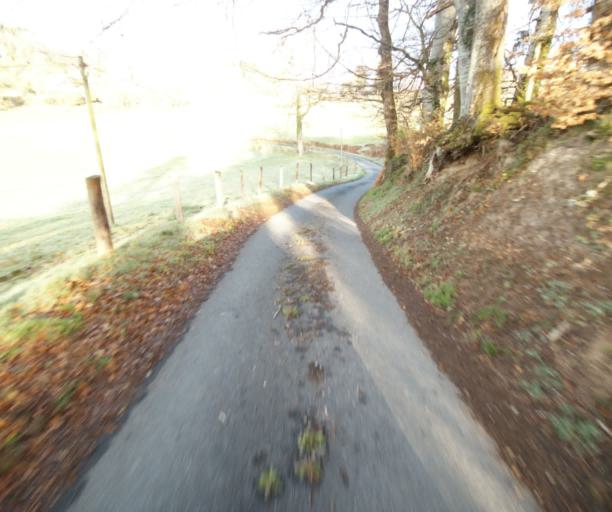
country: FR
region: Limousin
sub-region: Departement de la Correze
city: Correze
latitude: 45.3034
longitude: 1.8533
